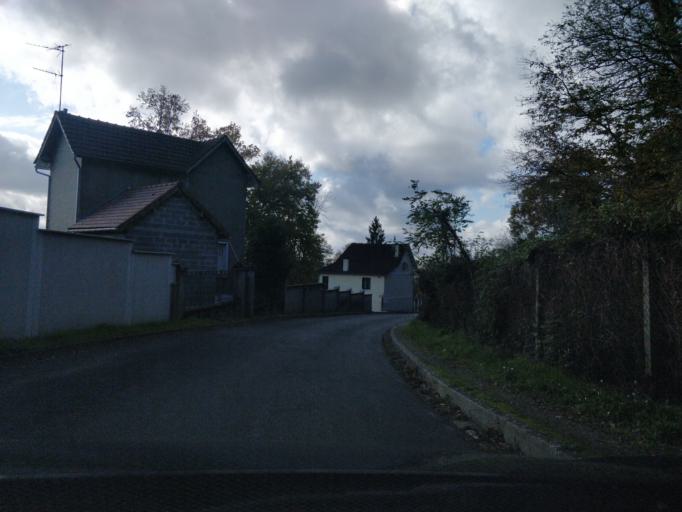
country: FR
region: Ile-de-France
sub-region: Departement de l'Essonne
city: Briis-sous-Forges
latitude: 48.6256
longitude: 2.1301
